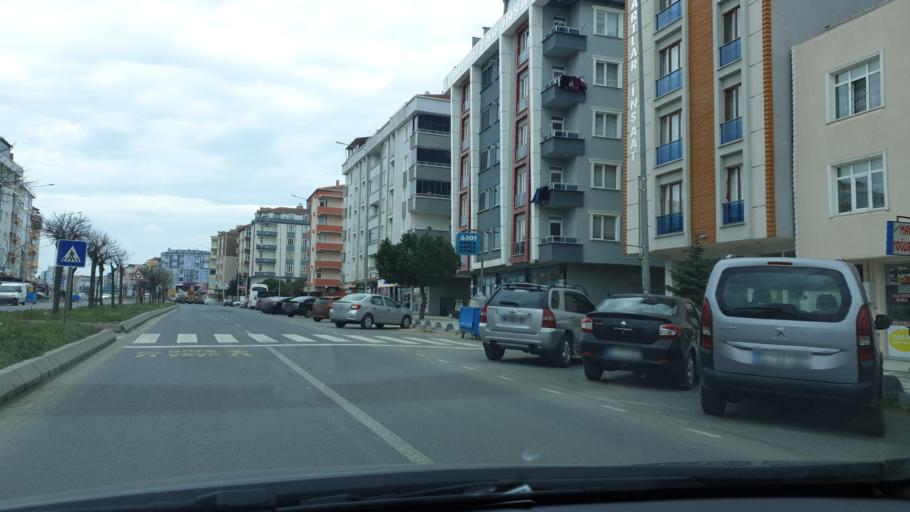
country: TR
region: Tekirdag
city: Cerkezkoey
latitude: 41.2861
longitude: 27.9885
